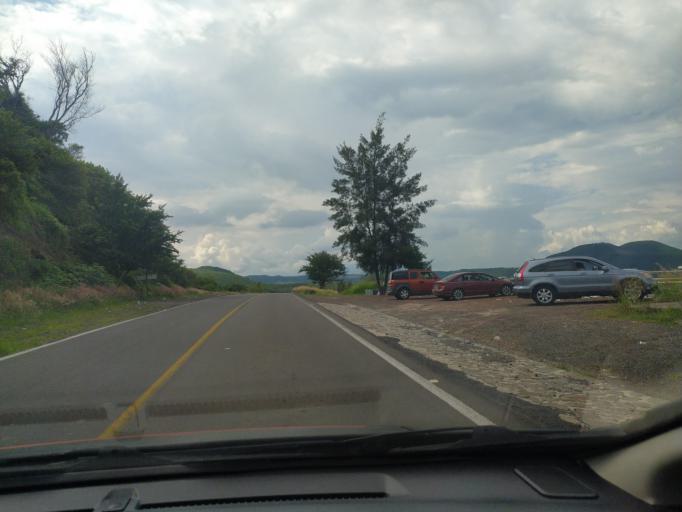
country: MX
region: Jalisco
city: Villa Corona
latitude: 20.3959
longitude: -103.6787
